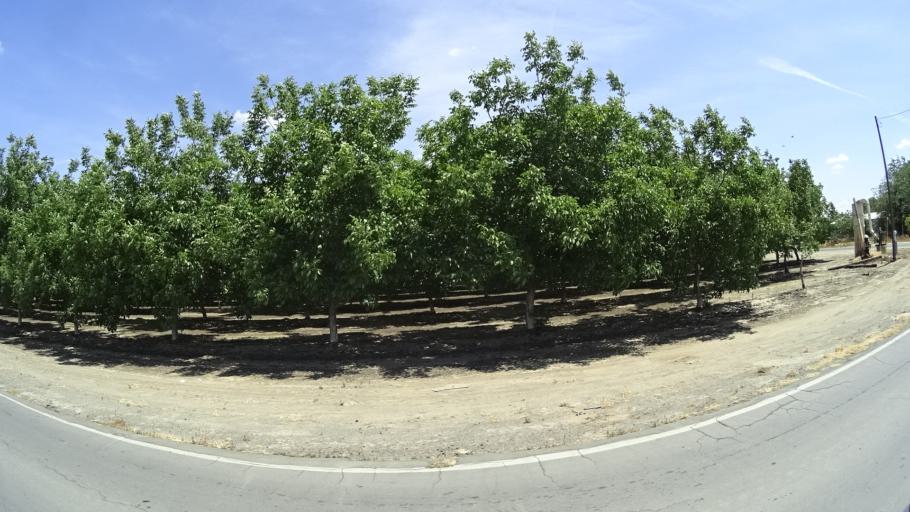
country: US
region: California
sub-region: Kings County
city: Home Garden
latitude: 36.2842
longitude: -119.6728
